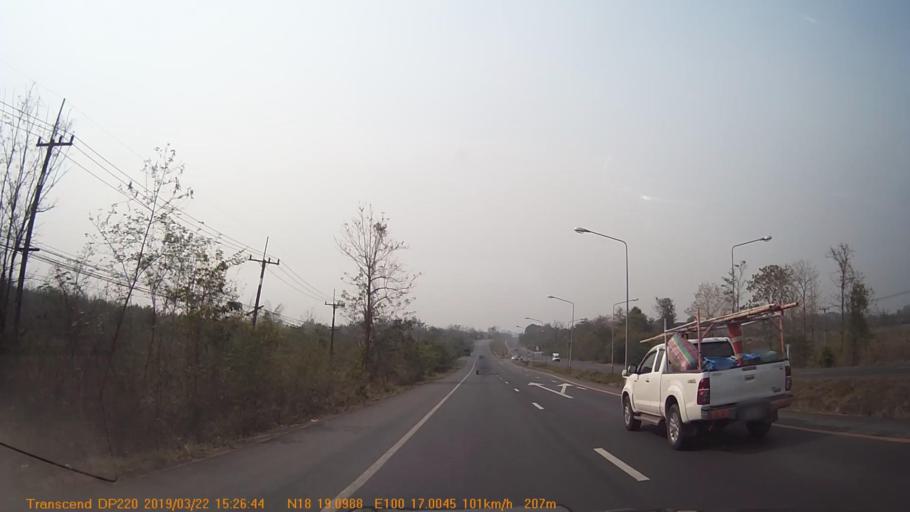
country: TH
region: Phrae
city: Rong Kwang
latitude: 18.3185
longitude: 100.2832
